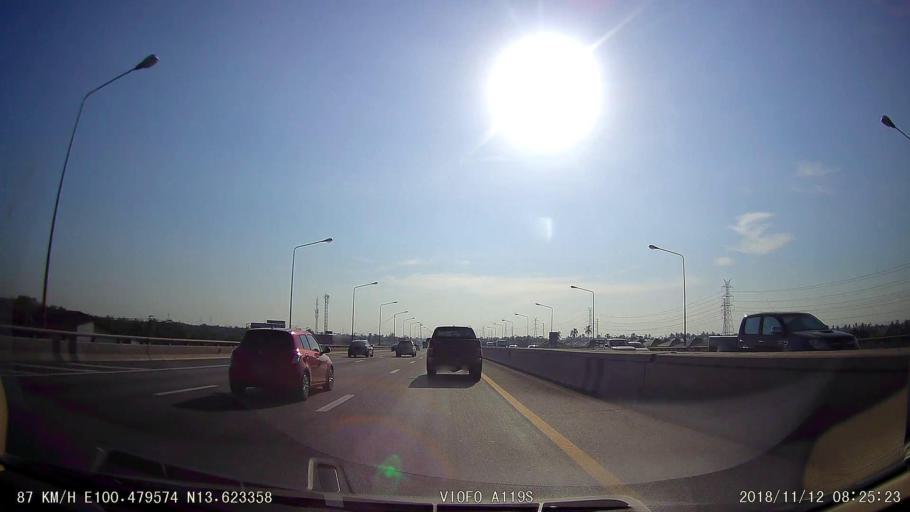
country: TH
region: Bangkok
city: Thung Khru
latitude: 13.6233
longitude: 100.4798
